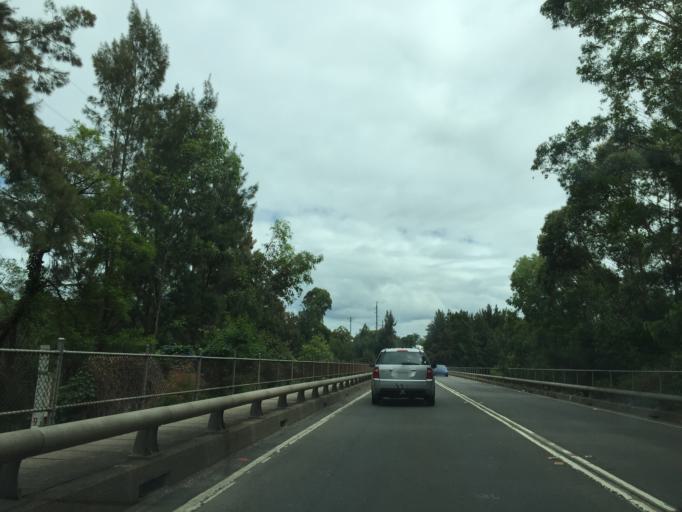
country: AU
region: New South Wales
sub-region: Hawkesbury
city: Richmond
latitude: -33.5858
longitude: 150.7249
